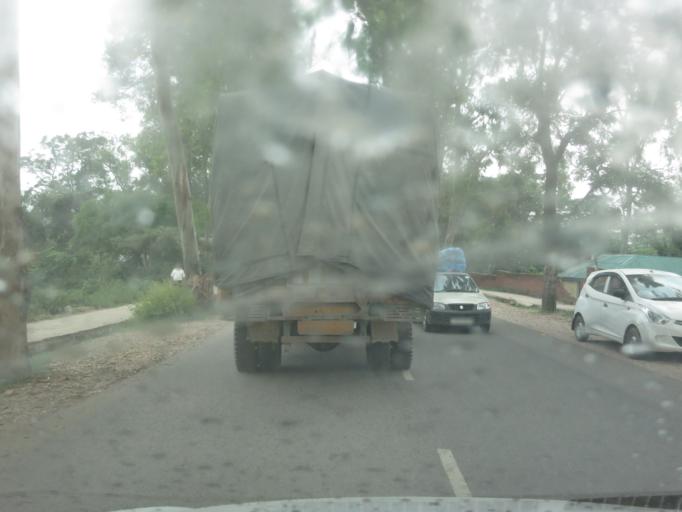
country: IN
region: Himachal Pradesh
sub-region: Mandi
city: Sundarnagar
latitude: 31.5183
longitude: 76.8845
